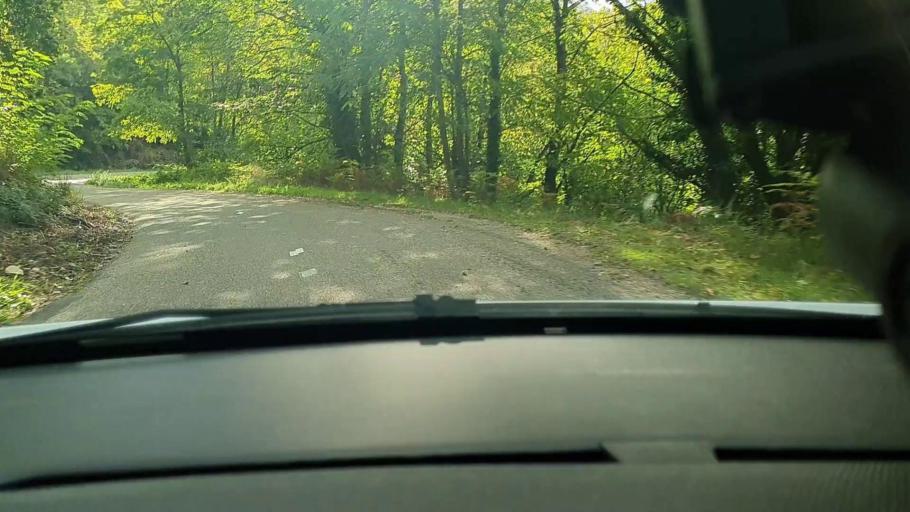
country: FR
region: Languedoc-Roussillon
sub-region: Departement du Gard
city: Besseges
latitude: 44.3828
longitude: 3.9851
